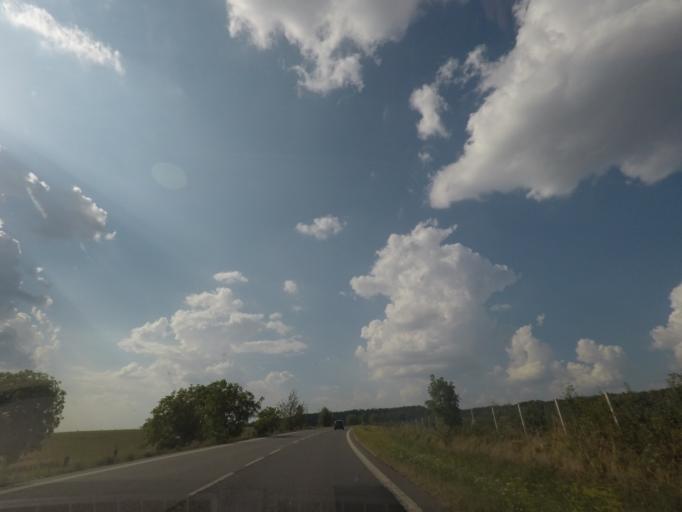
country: CZ
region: Kralovehradecky
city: Dvur Kralove nad Labem
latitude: 50.4285
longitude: 15.8705
